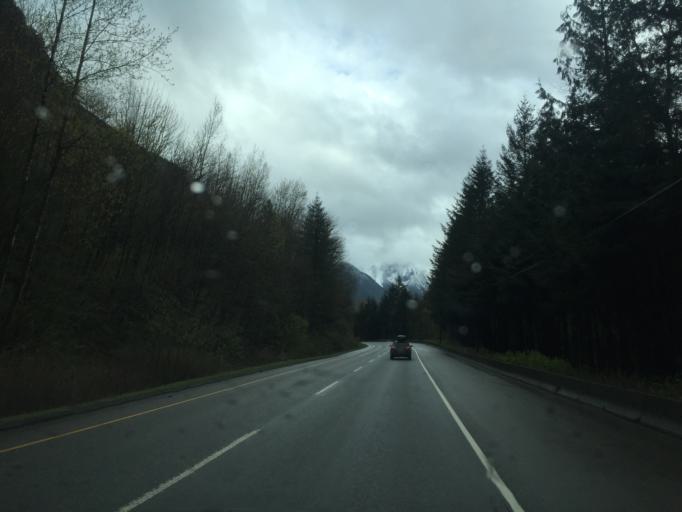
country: CA
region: British Columbia
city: Agassiz
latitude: 49.2666
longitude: -121.6763
